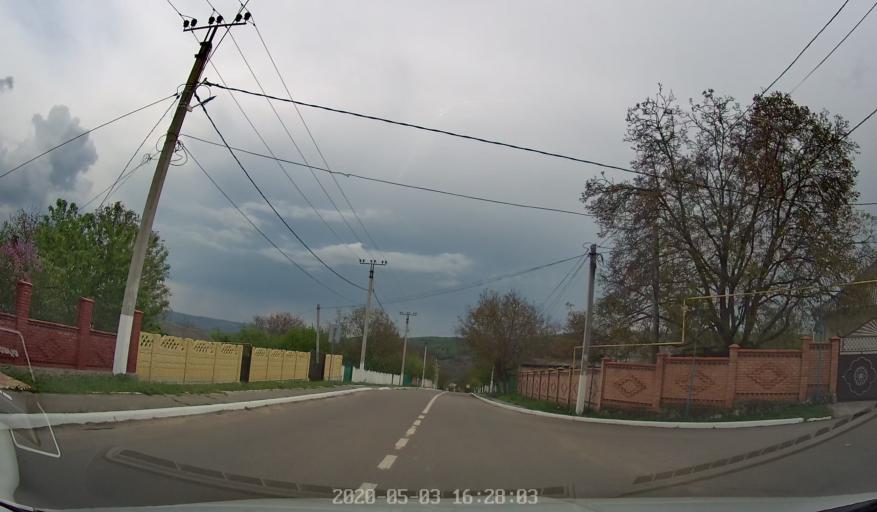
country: MD
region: Calarasi
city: Calarasi
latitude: 47.1953
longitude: 28.3499
